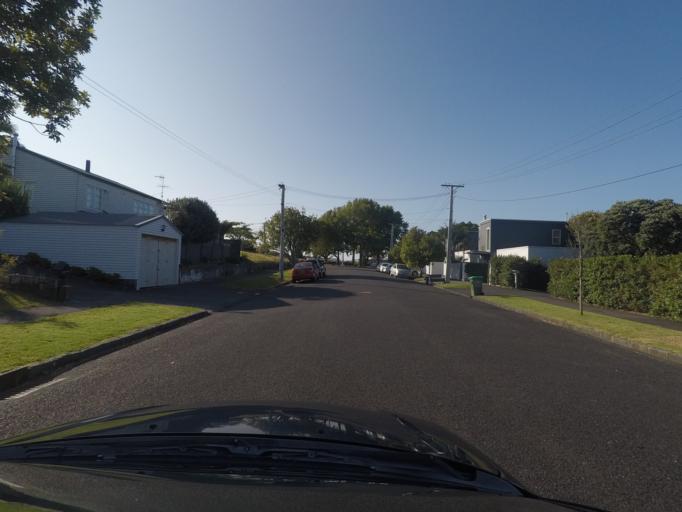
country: NZ
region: Auckland
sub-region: Auckland
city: Rosebank
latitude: -36.8638
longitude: 174.7138
